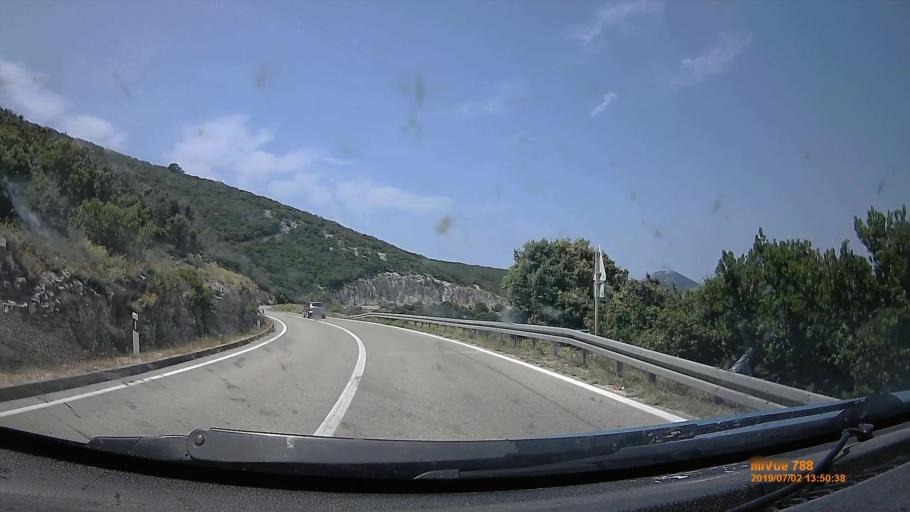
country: HR
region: Primorsko-Goranska
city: Mali Losinj
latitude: 44.5985
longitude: 14.4091
